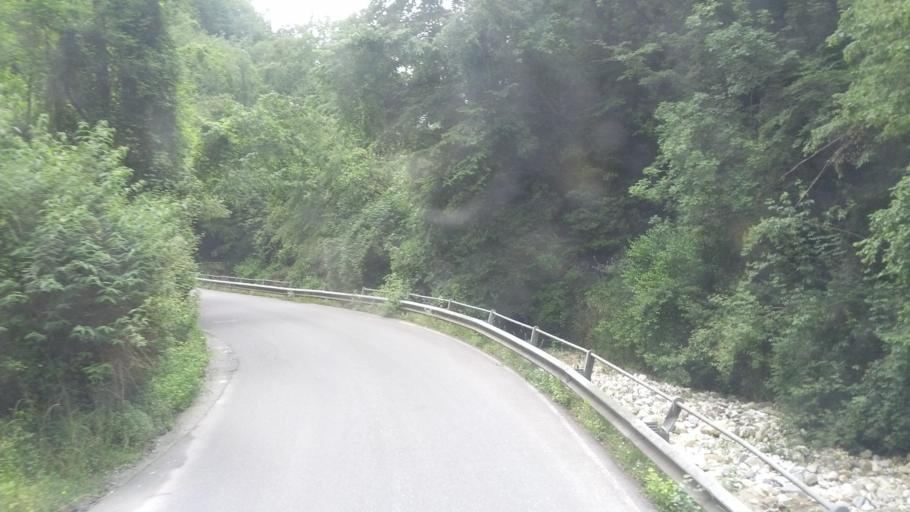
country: IT
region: Tuscany
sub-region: Provincia di Massa-Carrara
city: Carrara
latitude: 44.0862
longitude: 10.1034
